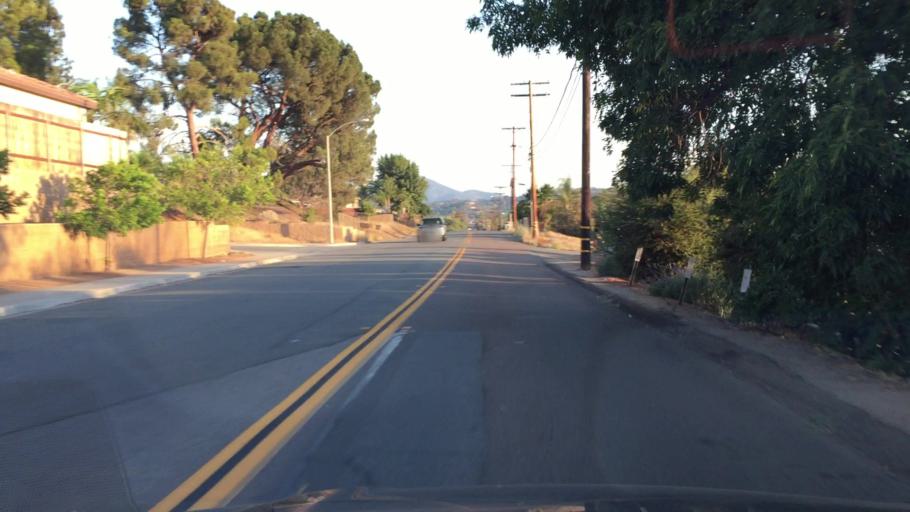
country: US
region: California
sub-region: San Diego County
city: Bostonia
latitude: 32.8178
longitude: -116.9447
